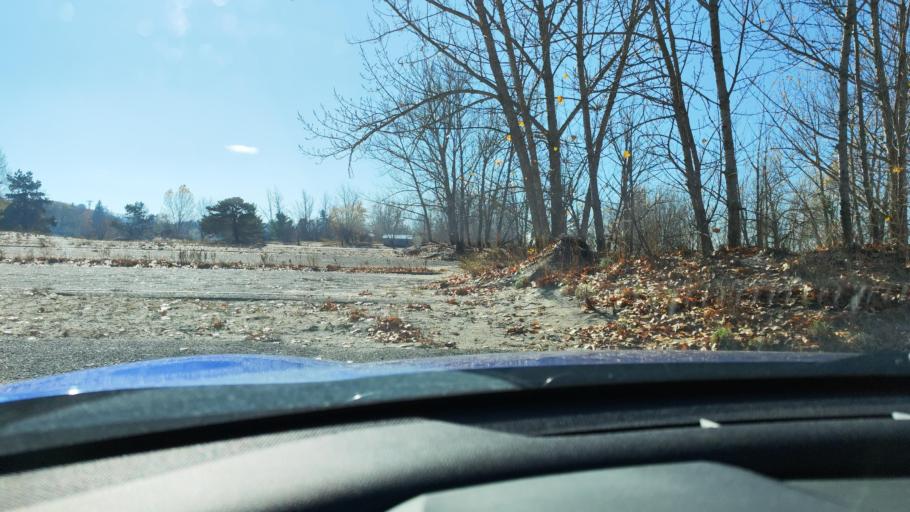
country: CA
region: Ontario
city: Wasaga Beach
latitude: 44.5306
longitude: -80.0135
